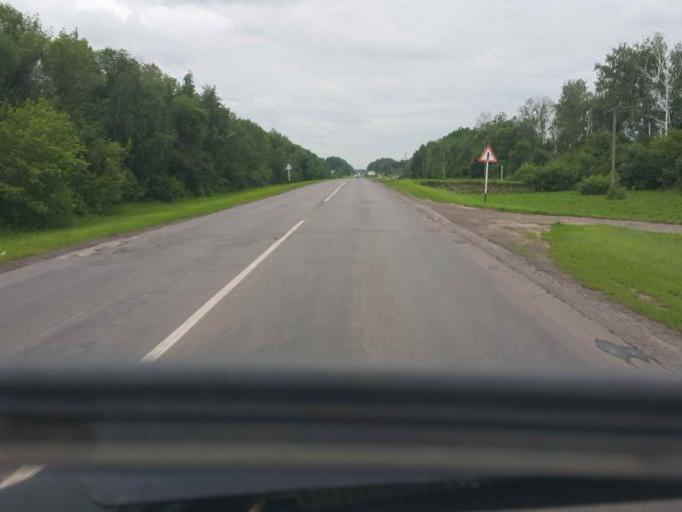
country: RU
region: Tambov
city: Zavoronezhskoye
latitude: 52.9046
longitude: 40.6162
